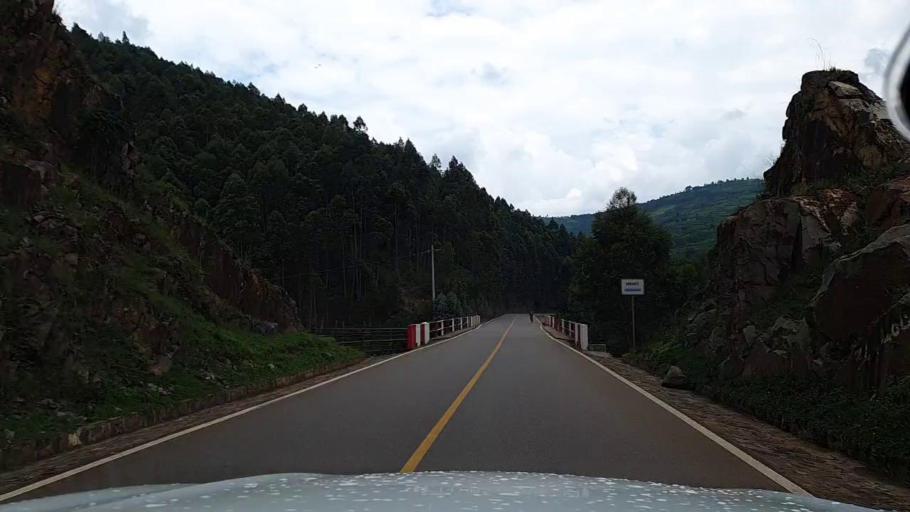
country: RW
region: Northern Province
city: Byumba
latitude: -1.7176
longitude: 30.1203
